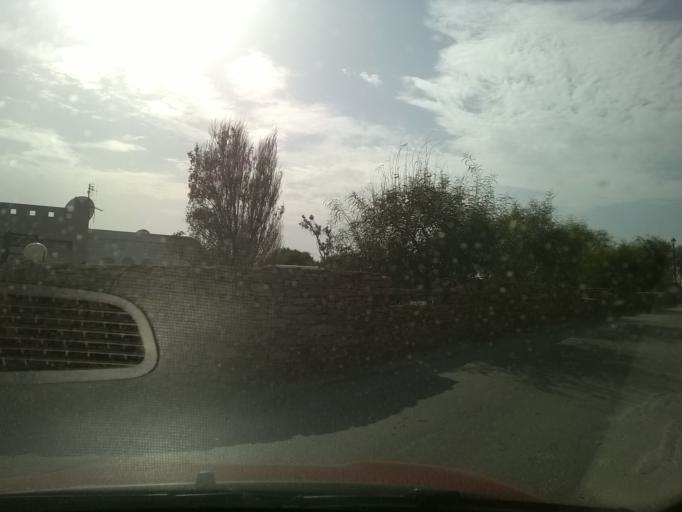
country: GR
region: South Aegean
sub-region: Nomos Kykladon
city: Naxos
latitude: 37.0825
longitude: 25.3473
